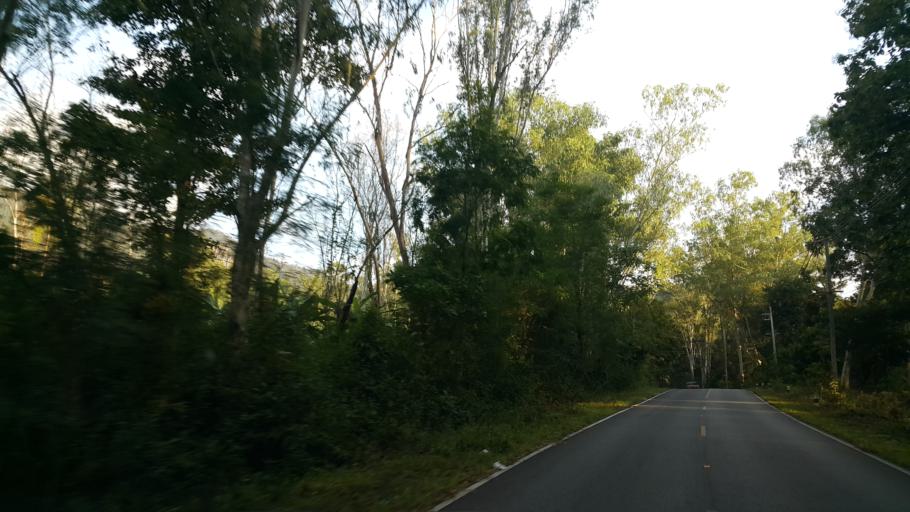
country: TH
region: Chiang Mai
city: Mae On
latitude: 18.7375
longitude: 99.2610
